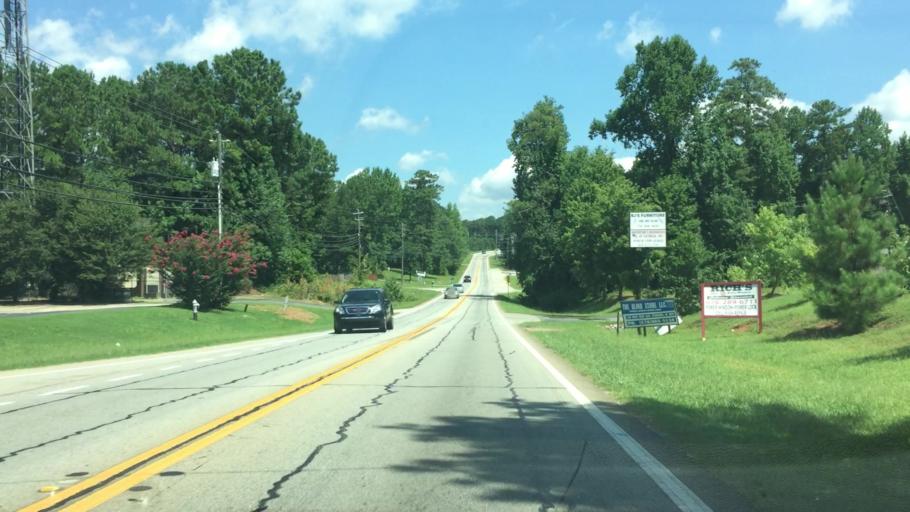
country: US
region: Georgia
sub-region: Henry County
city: Stockbridge
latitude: 33.5344
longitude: -84.1996
